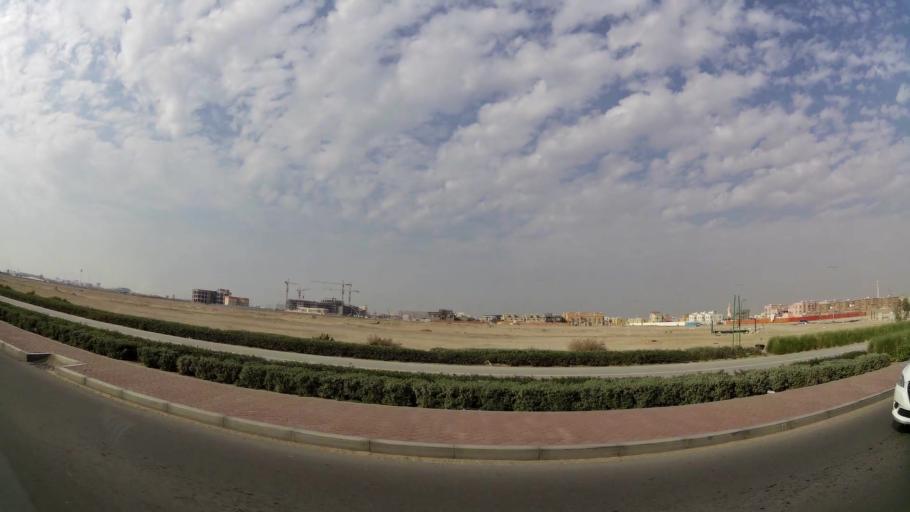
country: AE
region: Abu Dhabi
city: Abu Dhabi
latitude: 24.3478
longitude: 54.5410
